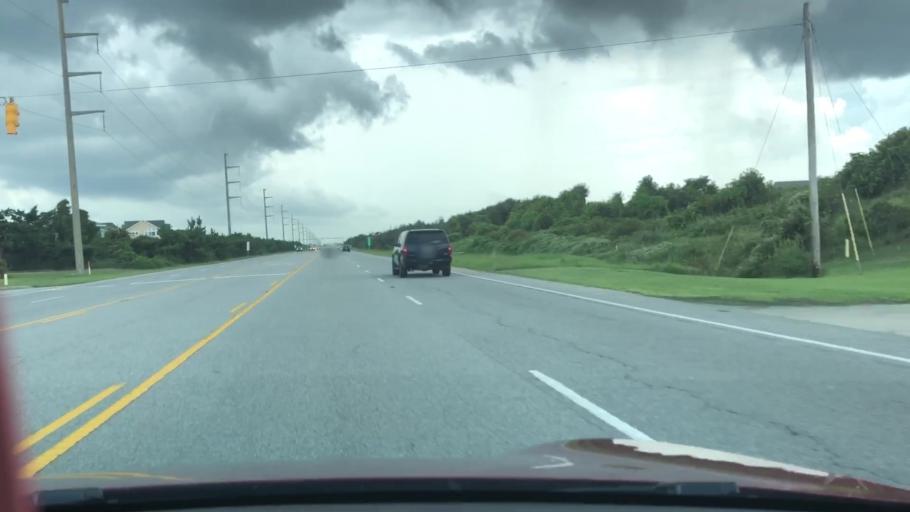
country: US
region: North Carolina
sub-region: Dare County
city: Nags Head
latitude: 35.9343
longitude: -75.6136
